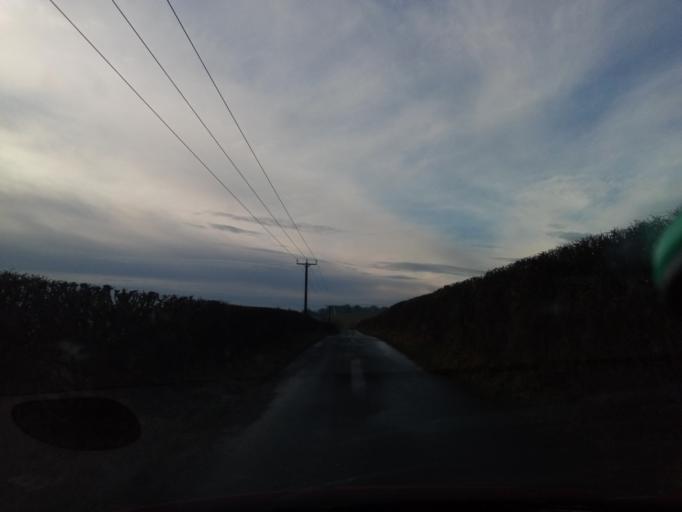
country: GB
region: Scotland
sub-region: The Scottish Borders
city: Hawick
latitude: 55.4487
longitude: -2.7404
